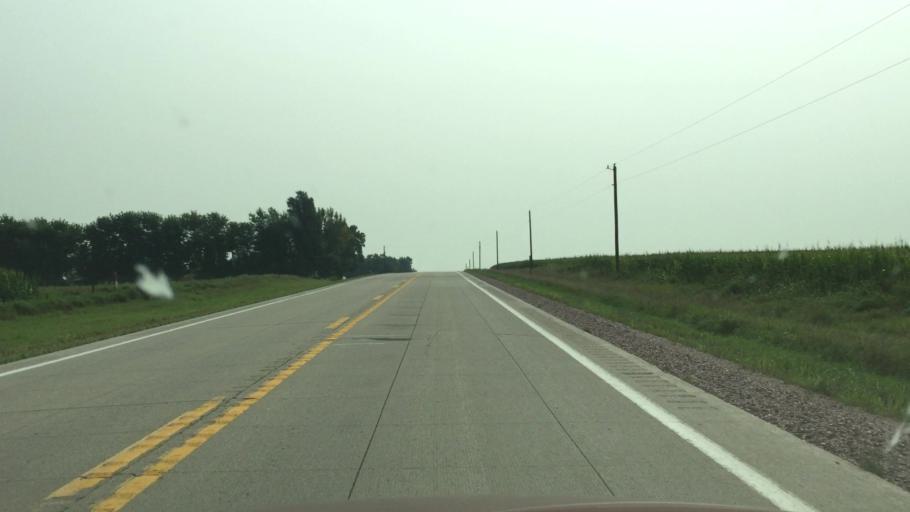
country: US
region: Iowa
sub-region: Osceola County
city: Sibley
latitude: 43.4327
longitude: -95.6984
